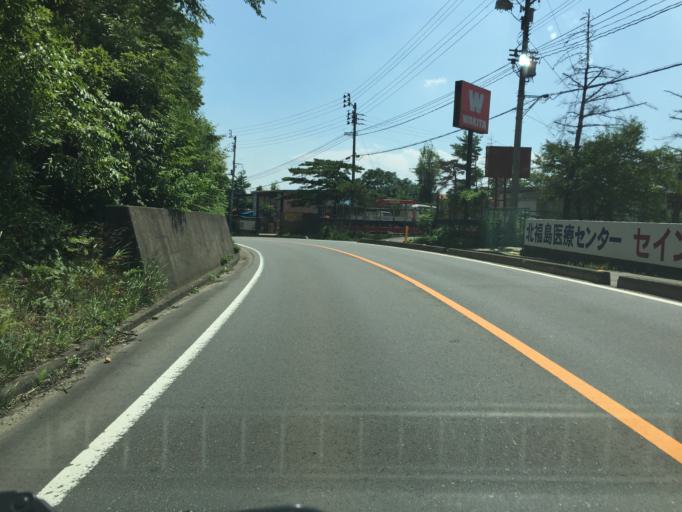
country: JP
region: Fukushima
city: Hobaramachi
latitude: 37.8000
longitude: 140.5172
